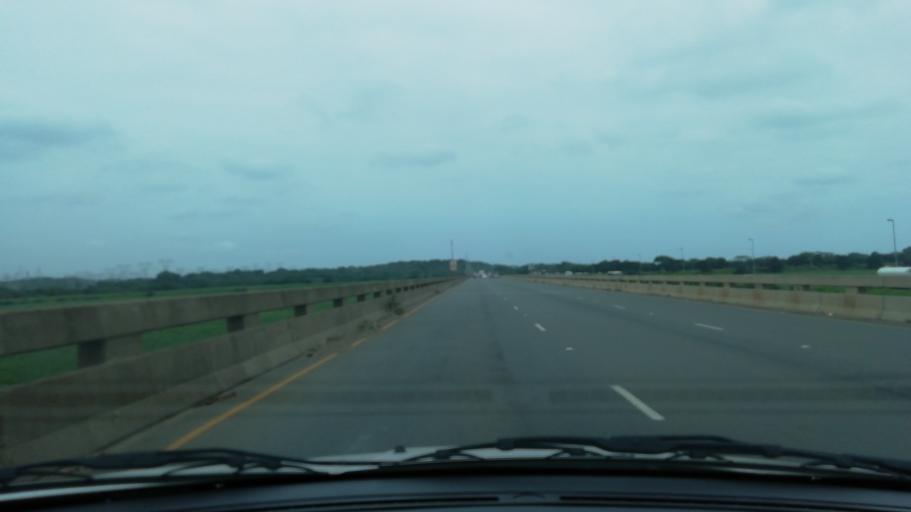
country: ZA
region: KwaZulu-Natal
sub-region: uThungulu District Municipality
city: Empangeni
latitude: -28.7738
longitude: 31.9536
